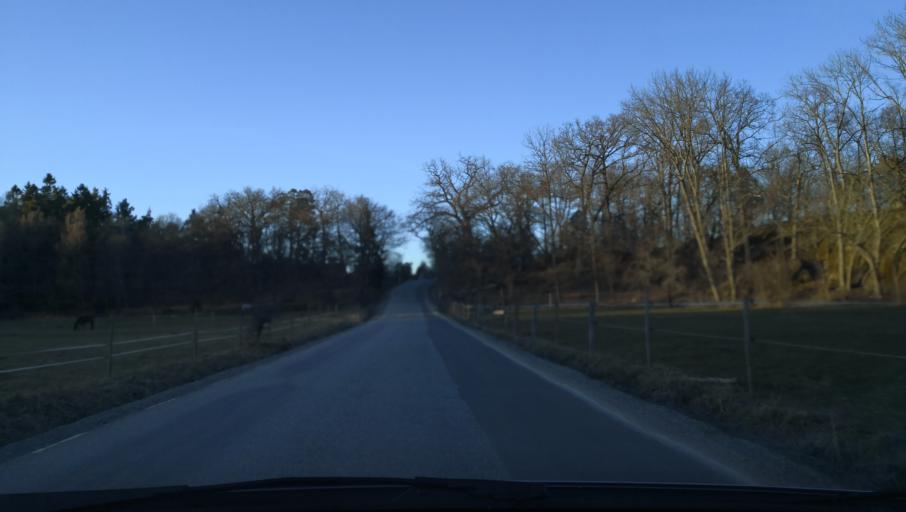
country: SE
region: Stockholm
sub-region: Varmdo Kommun
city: Mortnas
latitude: 59.3340
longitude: 18.4402
